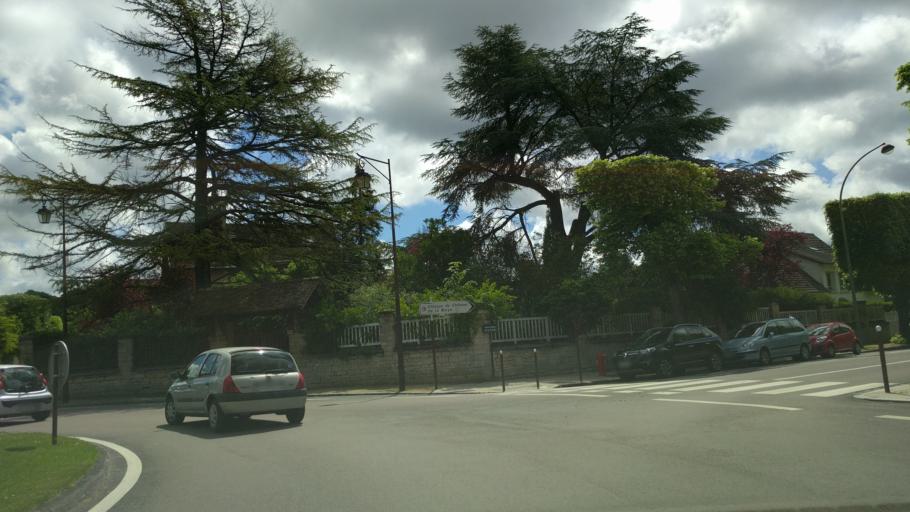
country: FR
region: Ile-de-France
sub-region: Departement des Yvelines
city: Le Chesnay
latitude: 48.8203
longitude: 2.1419
